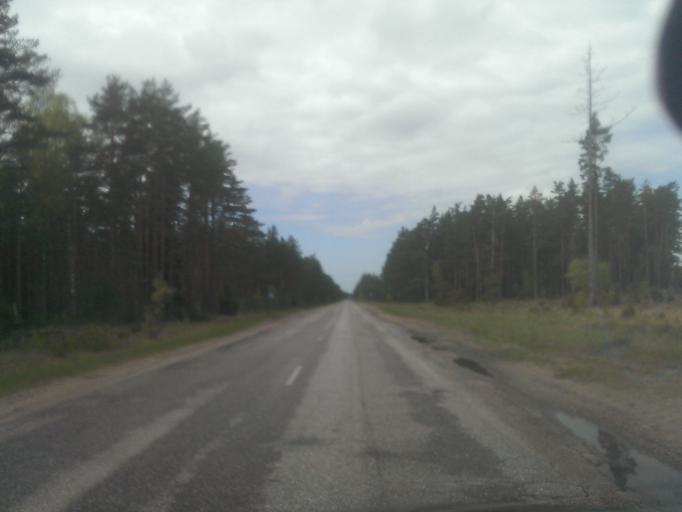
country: LV
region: Ventspils Rajons
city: Piltene
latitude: 57.1255
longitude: 21.7379
